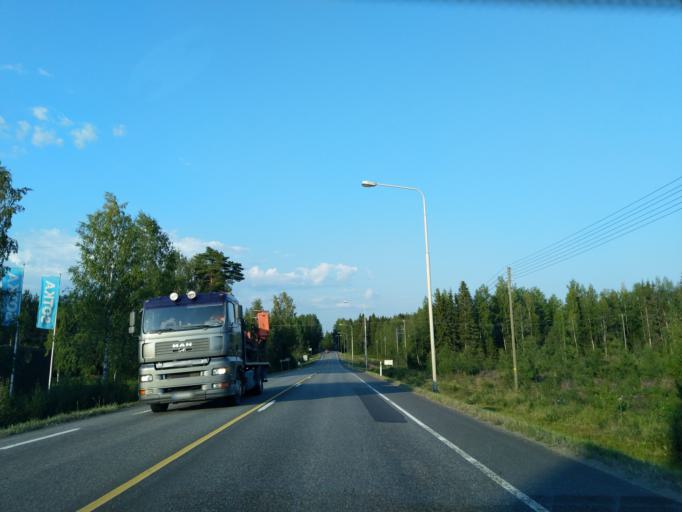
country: FI
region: Satakunta
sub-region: Pohjois-Satakunta
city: Kankaanpaeae
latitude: 61.8147
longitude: 22.3528
